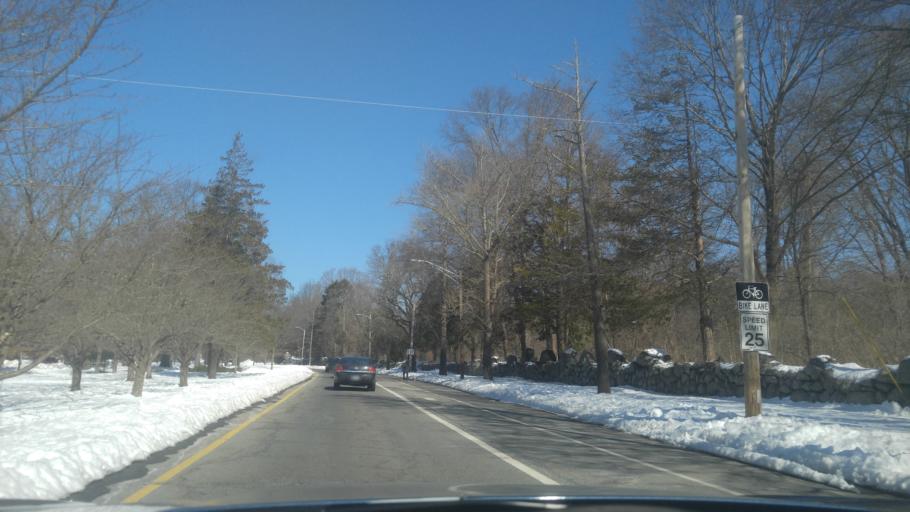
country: US
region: Rhode Island
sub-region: Providence County
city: Pawtucket
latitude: 41.8502
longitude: -71.3869
